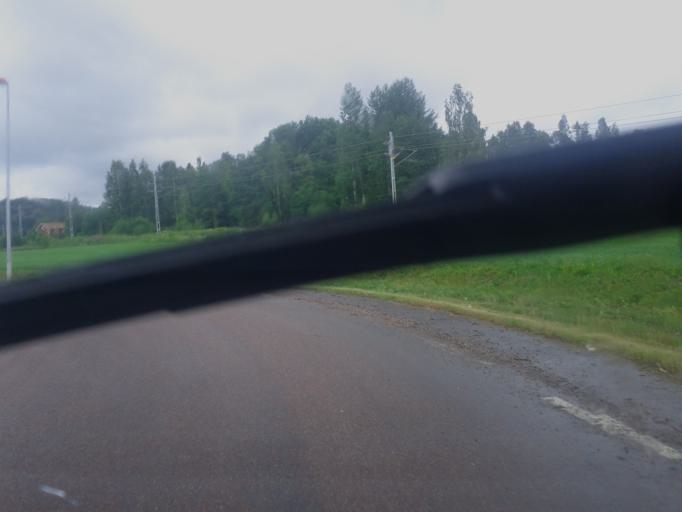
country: SE
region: Vaesternorrland
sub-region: Sundsvalls Kommun
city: Sundsvall
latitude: 62.4116
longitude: 17.2331
